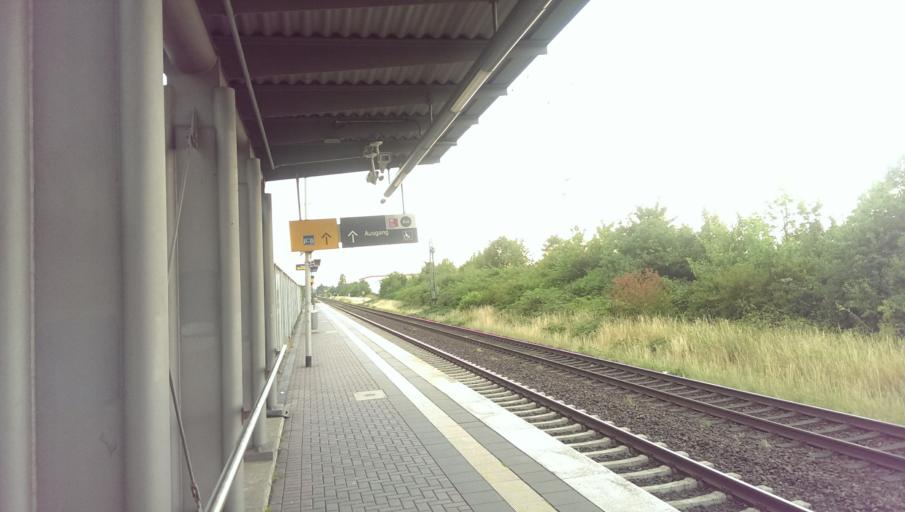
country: DE
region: North Rhine-Westphalia
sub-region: Regierungsbezirk Dusseldorf
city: Dusseldorf
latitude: 51.1426
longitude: 6.7564
